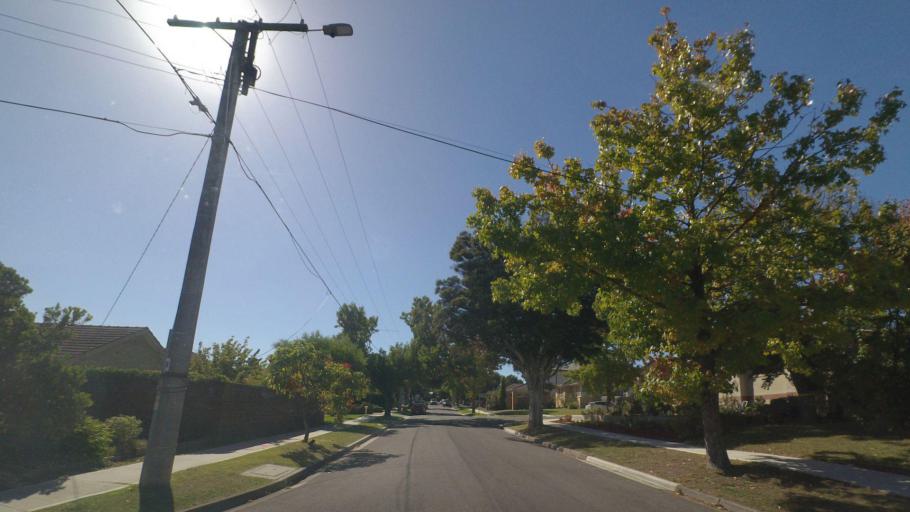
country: AU
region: Victoria
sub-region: Manningham
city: Donvale
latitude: -37.7968
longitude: 145.1739
